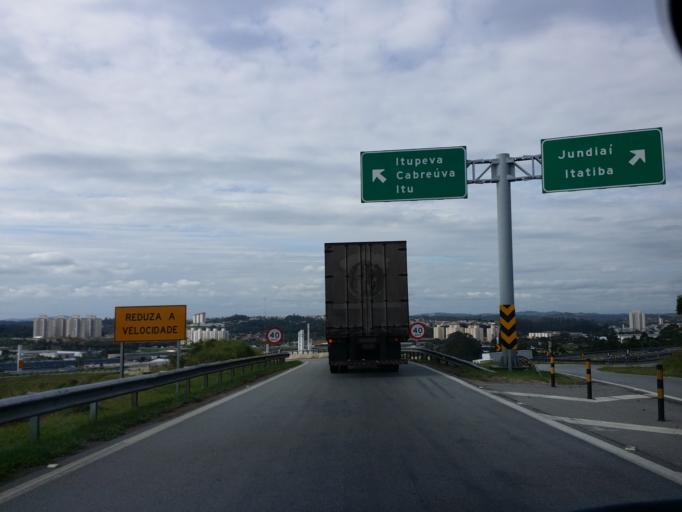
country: BR
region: Sao Paulo
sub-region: Jundiai
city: Jundiai
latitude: -23.1735
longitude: -46.9357
